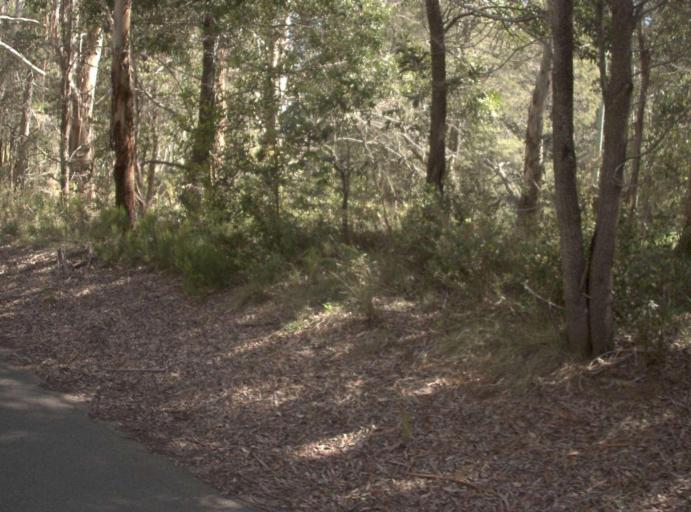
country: AU
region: New South Wales
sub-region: Bombala
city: Bombala
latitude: -37.2028
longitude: 148.7293
